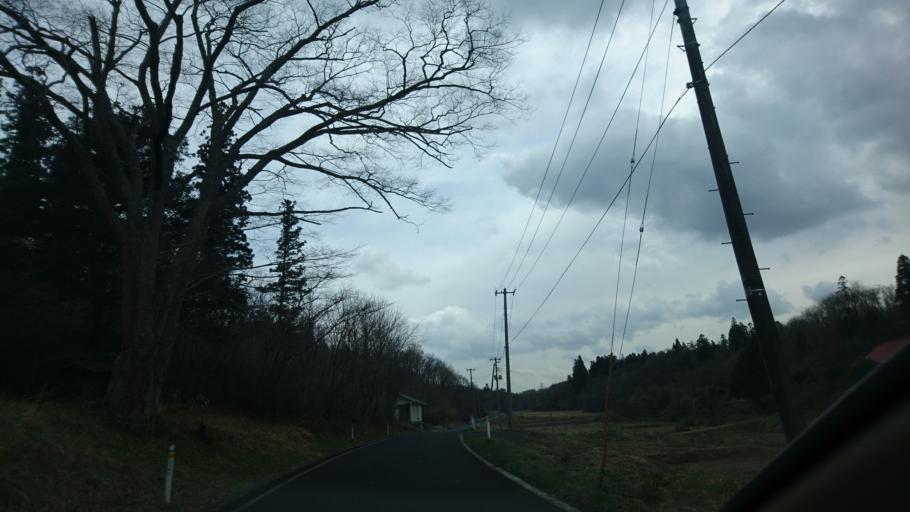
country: JP
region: Iwate
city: Ichinoseki
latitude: 38.8912
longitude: 141.1694
